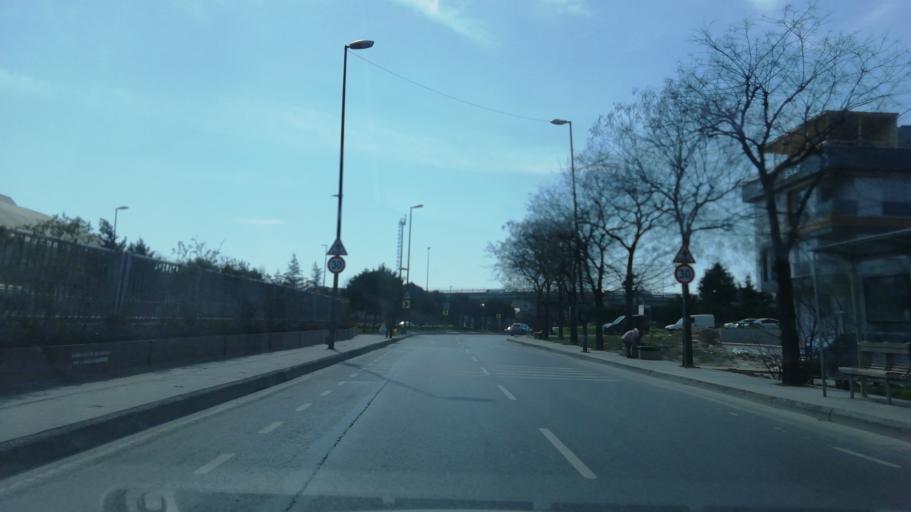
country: TR
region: Istanbul
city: Bahcelievler
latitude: 41.0147
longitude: 28.8483
